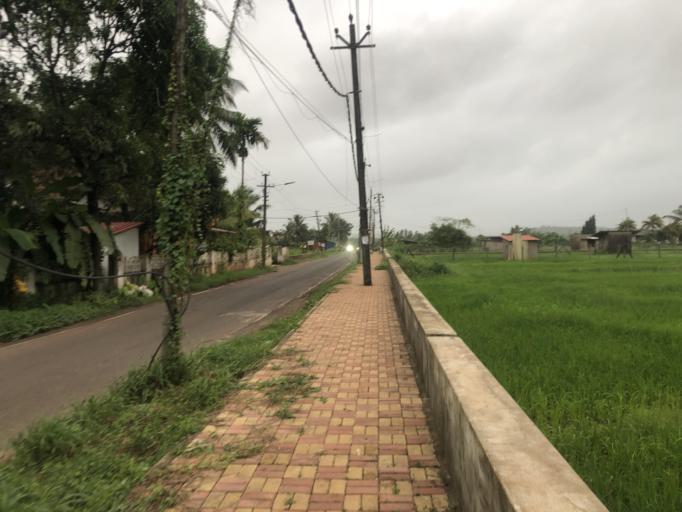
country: IN
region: Goa
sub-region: North Goa
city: Saligao
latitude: 15.5539
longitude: 73.8065
